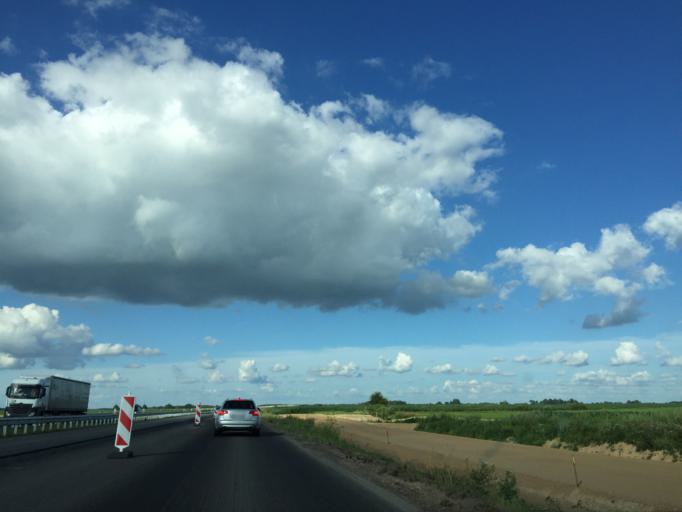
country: LT
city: Kazlu Ruda
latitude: 54.6949
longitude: 23.6037
